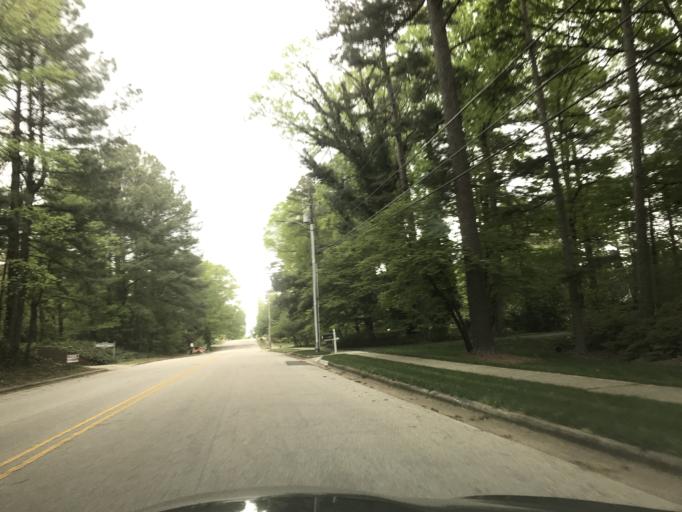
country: US
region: North Carolina
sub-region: Wake County
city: West Raleigh
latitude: 35.7813
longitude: -78.7128
